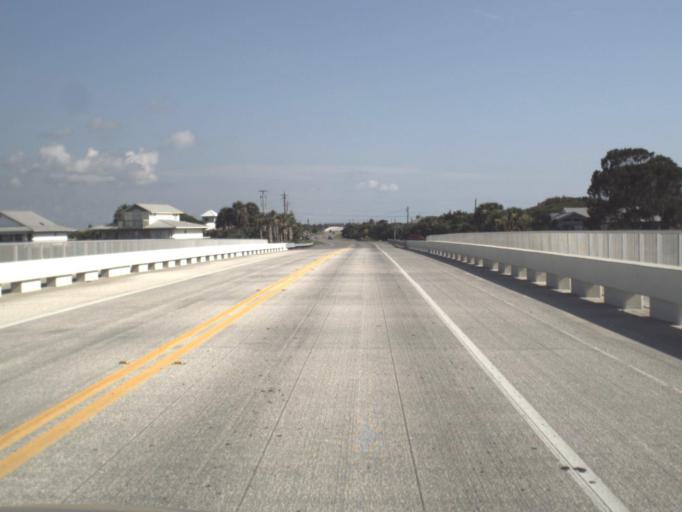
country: US
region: Florida
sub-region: Saint Johns County
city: Butler Beach
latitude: 29.6968
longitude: -81.2254
